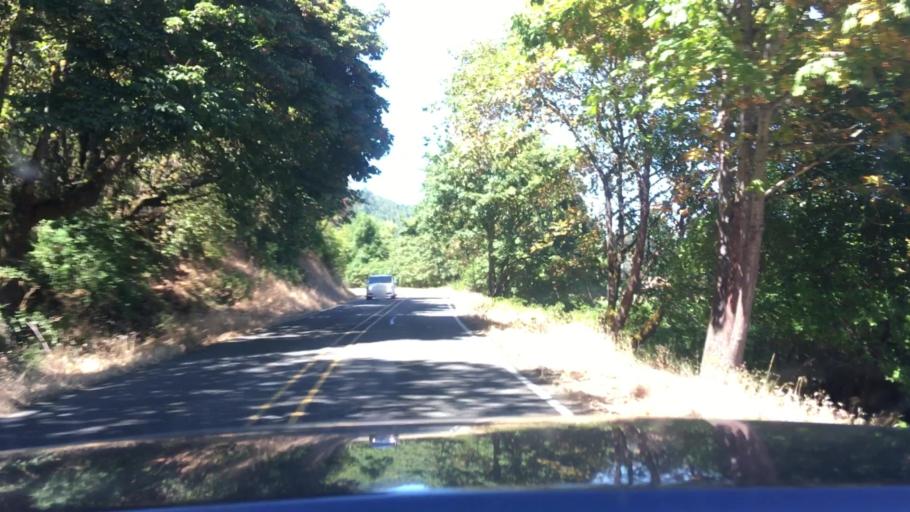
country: US
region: Oregon
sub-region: Douglas County
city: Winston
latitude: 43.1384
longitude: -123.4132
